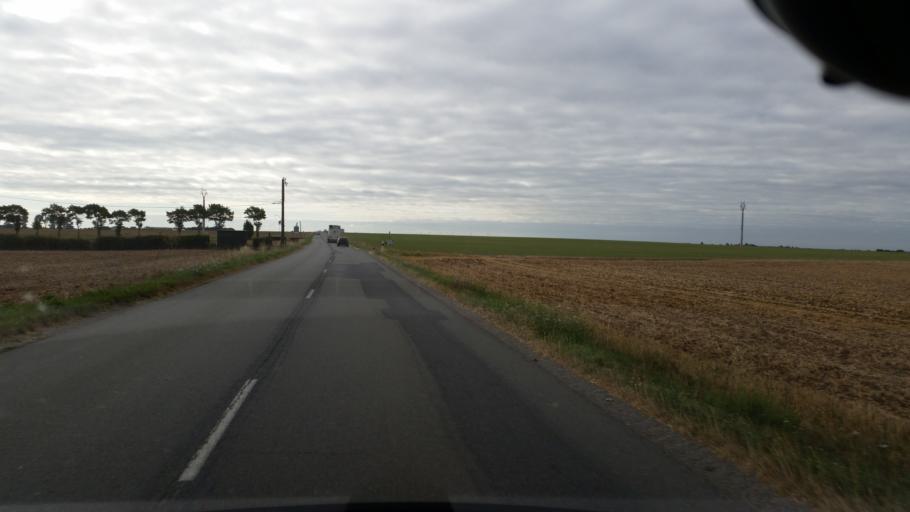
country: FR
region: Poitou-Charentes
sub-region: Departement de la Charente-Maritime
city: Marans
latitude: 46.2982
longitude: -0.9759
